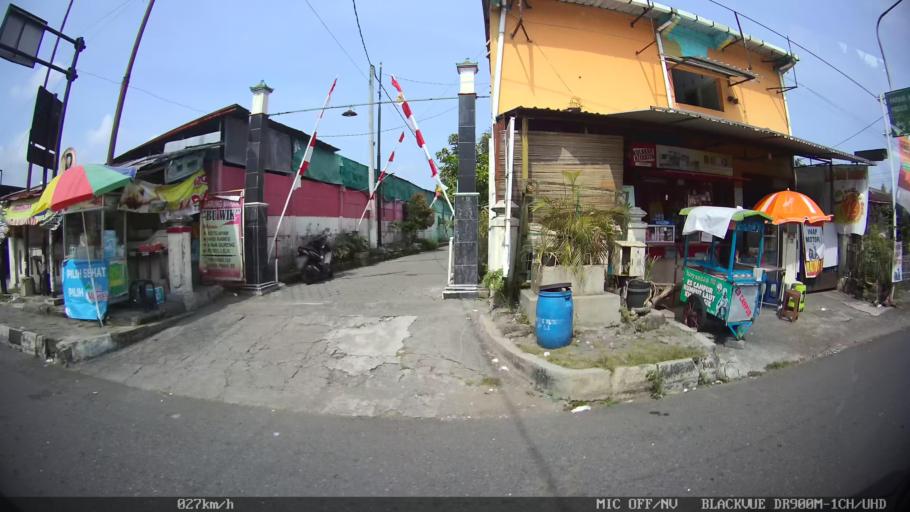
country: ID
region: Daerah Istimewa Yogyakarta
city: Depok
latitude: -7.7844
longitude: 110.4381
